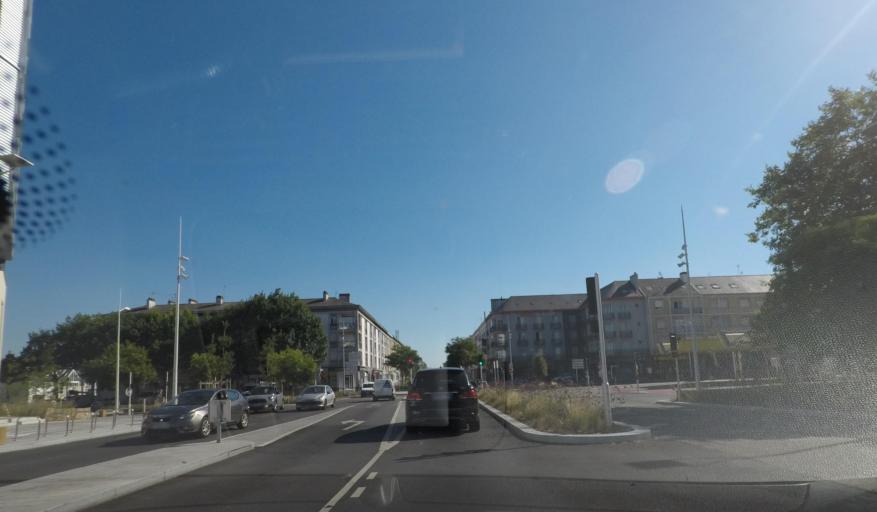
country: FR
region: Pays de la Loire
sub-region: Departement de la Loire-Atlantique
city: Saint-Nazaire
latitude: 47.2857
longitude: -2.2105
